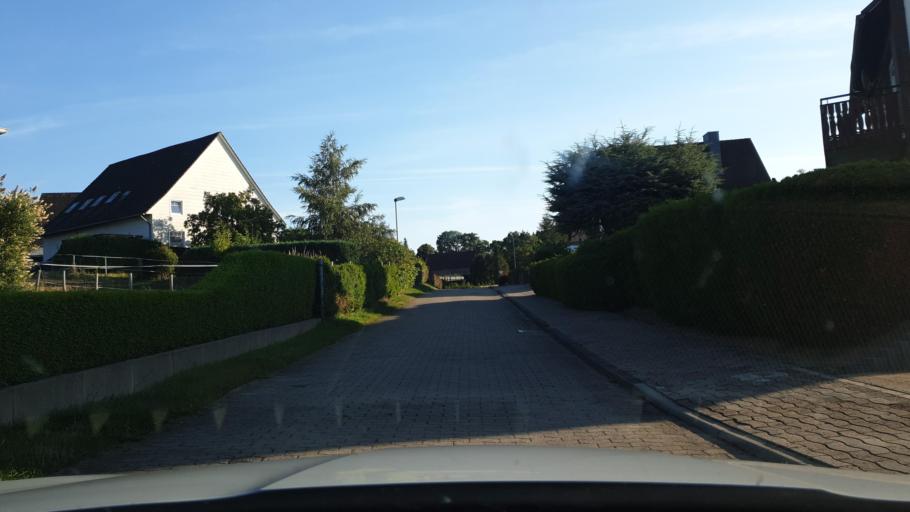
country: DE
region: Lower Saxony
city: Nienstadt
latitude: 52.2924
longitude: 9.1699
